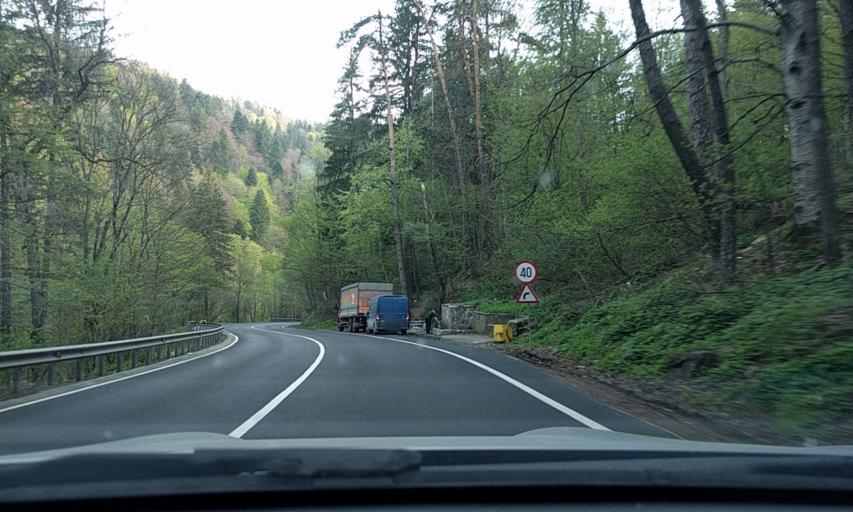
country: RO
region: Covasna
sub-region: Comuna Bretcu
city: Bretcu
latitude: 46.0850
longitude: 26.3998
